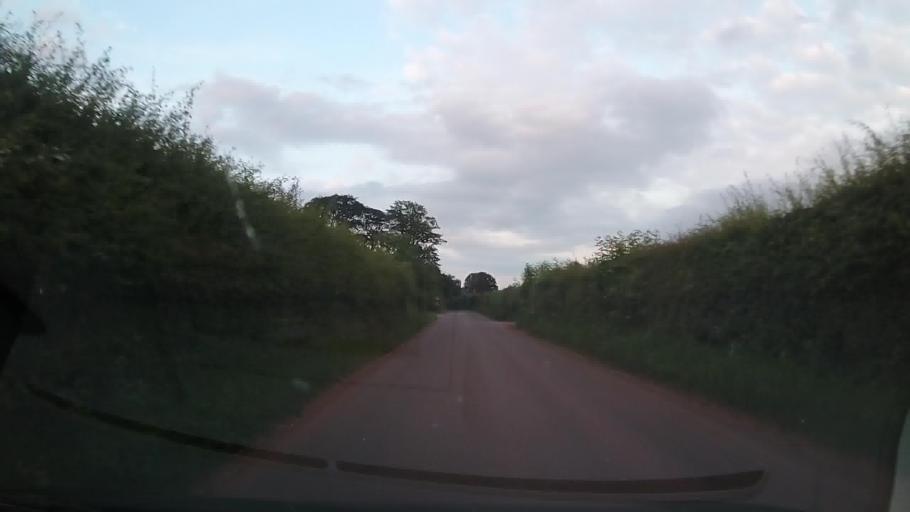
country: GB
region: England
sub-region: Shropshire
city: Clive
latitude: 52.8095
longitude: -2.7533
